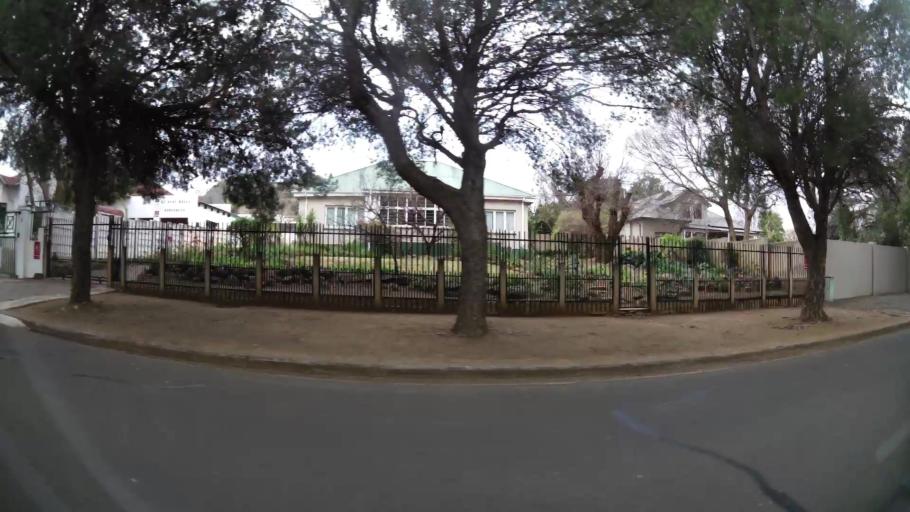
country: ZA
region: Orange Free State
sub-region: Mangaung Metropolitan Municipality
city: Bloemfontein
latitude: -29.1029
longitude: 26.2115
